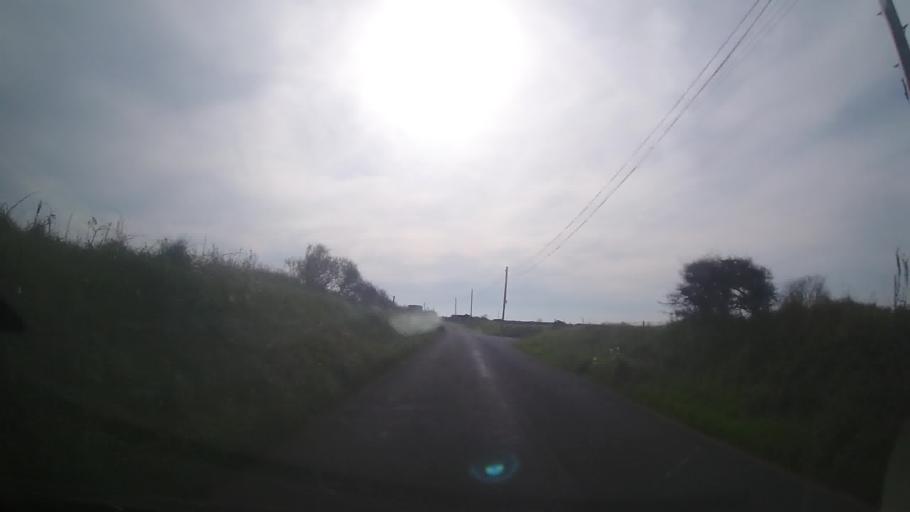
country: GB
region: Wales
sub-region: Pembrokeshire
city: Saint David's
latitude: 51.8899
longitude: -5.2554
